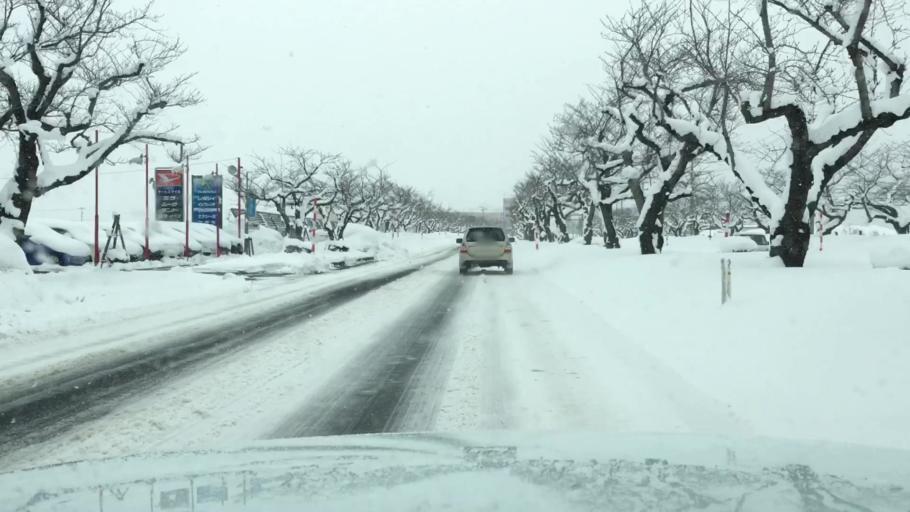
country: JP
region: Aomori
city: Hirosaki
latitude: 40.6376
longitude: 140.4889
